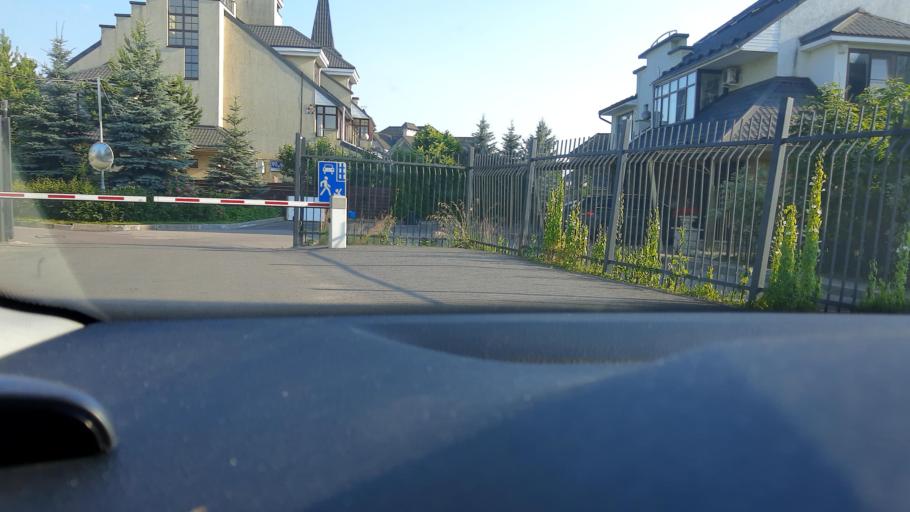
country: RU
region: Moskovskaya
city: Novopodrezkovo
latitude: 55.8973
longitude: 37.3755
